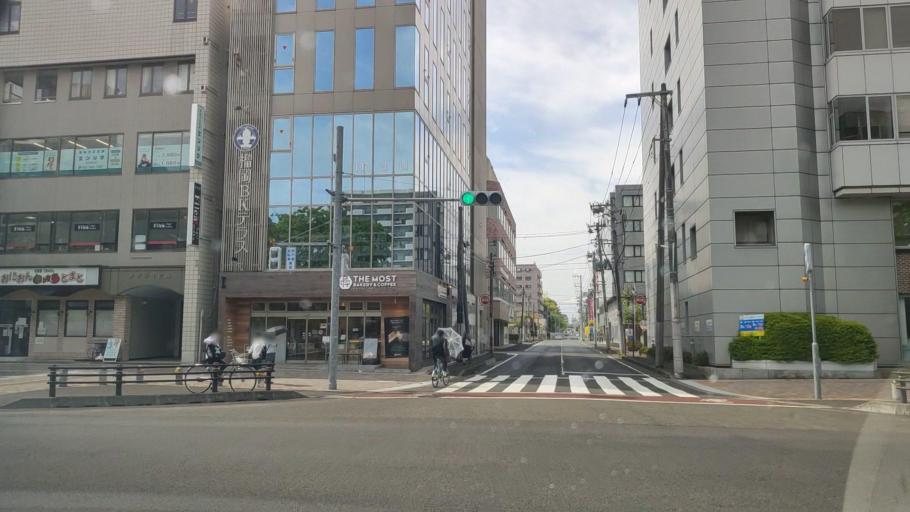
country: JP
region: Miyagi
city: Sendai-shi
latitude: 38.2595
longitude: 140.8892
